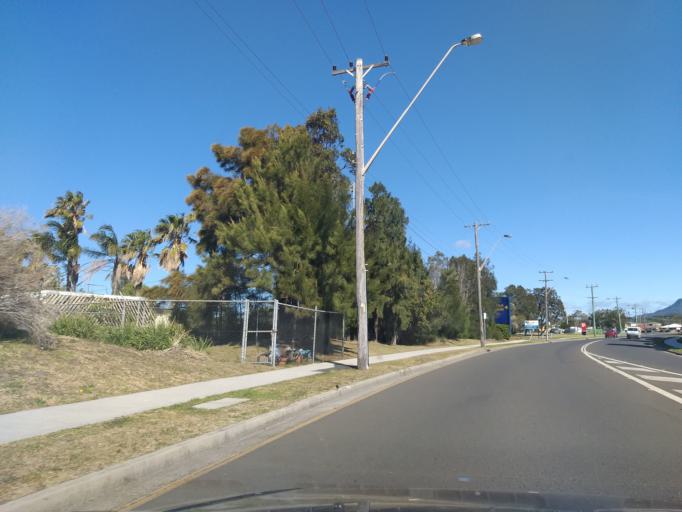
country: AU
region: New South Wales
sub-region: Wollongong
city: Corrimal
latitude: -34.3897
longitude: 150.9051
